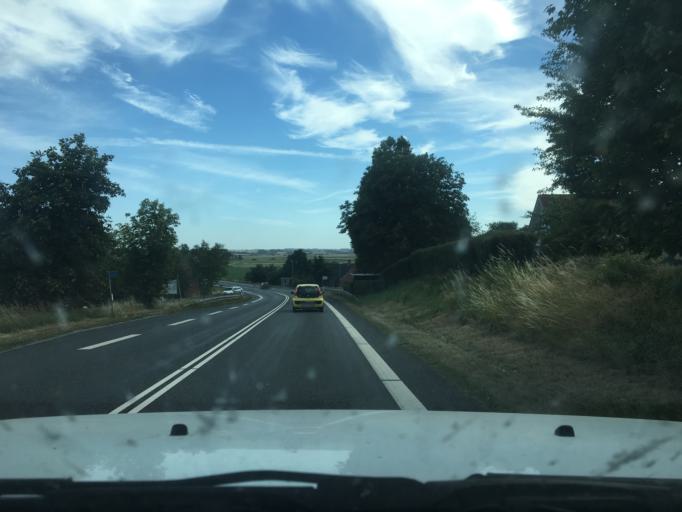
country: DK
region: Central Jutland
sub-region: Viborg Kommune
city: Viborg
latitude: 56.5767
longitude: 9.3773
